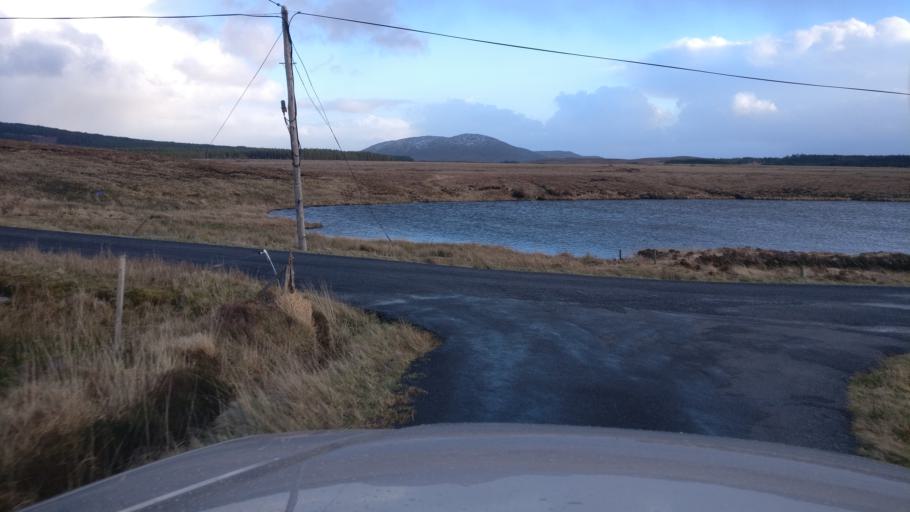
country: IE
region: Connaught
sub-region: County Galway
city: Clifden
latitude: 53.4727
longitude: -9.6911
